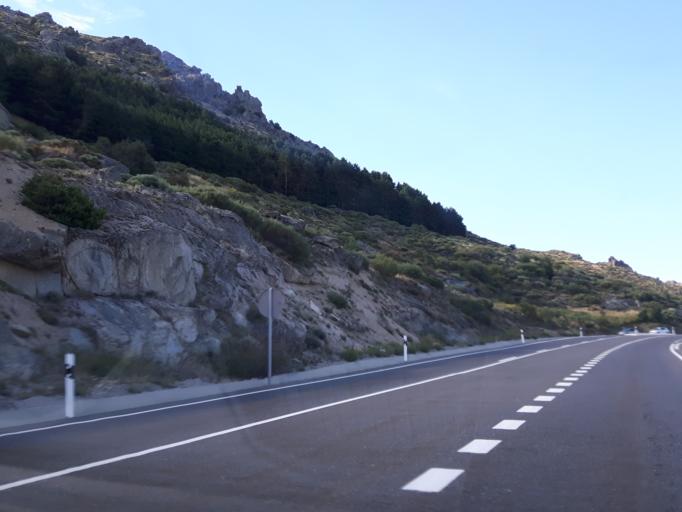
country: ES
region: Castille and Leon
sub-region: Provincia de Avila
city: Mengamunoz
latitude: 40.4854
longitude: -5.0060
